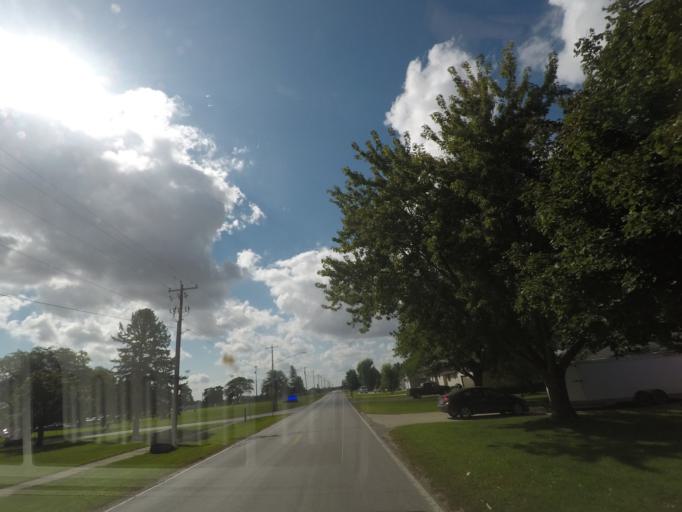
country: US
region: Iowa
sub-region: Story County
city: Nevada
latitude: 42.0116
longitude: -93.3192
